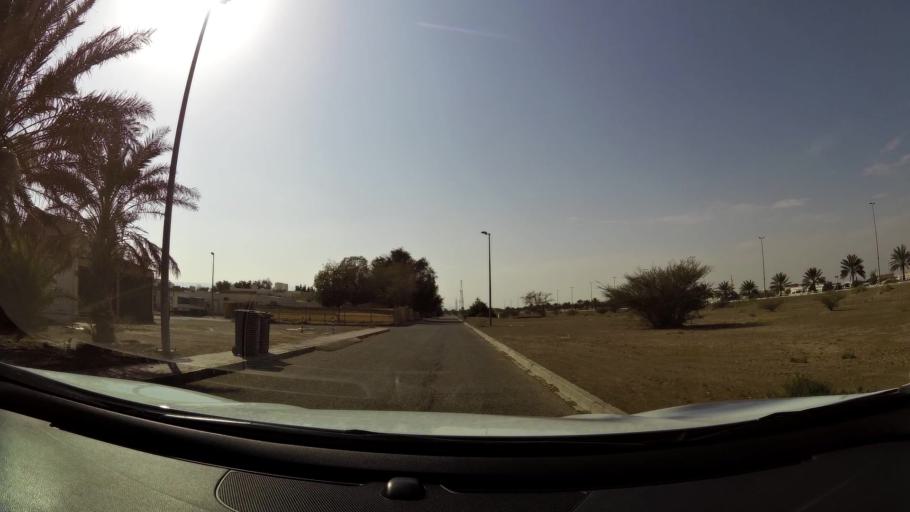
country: AE
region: Abu Dhabi
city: Al Ain
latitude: 24.0934
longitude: 55.9274
